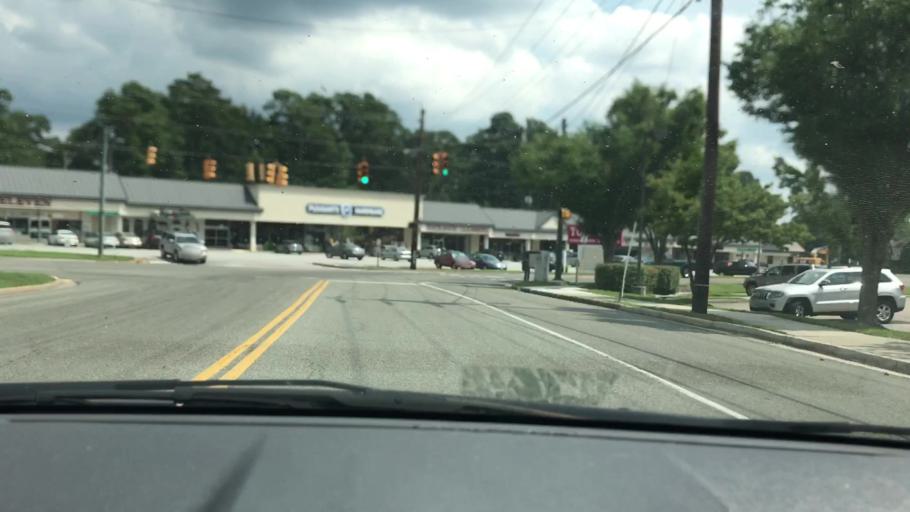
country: US
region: Virginia
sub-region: Henrico County
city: Tuckahoe
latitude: 37.5827
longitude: -77.5553
